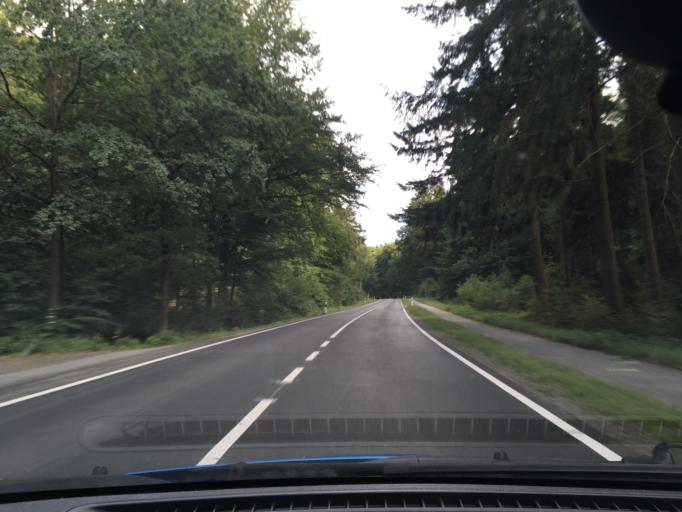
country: DE
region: Lower Saxony
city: Buchholz in der Nordheide
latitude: 53.4074
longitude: 9.8627
